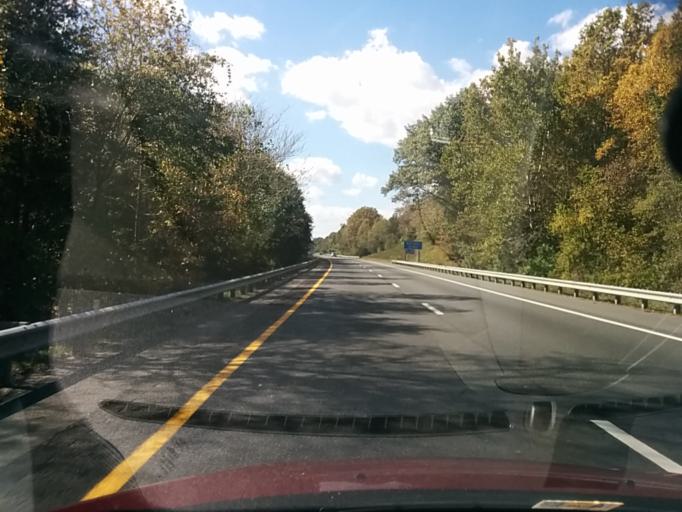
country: US
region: Virginia
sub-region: Albemarle County
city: Crozet
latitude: 38.0358
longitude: -78.6147
